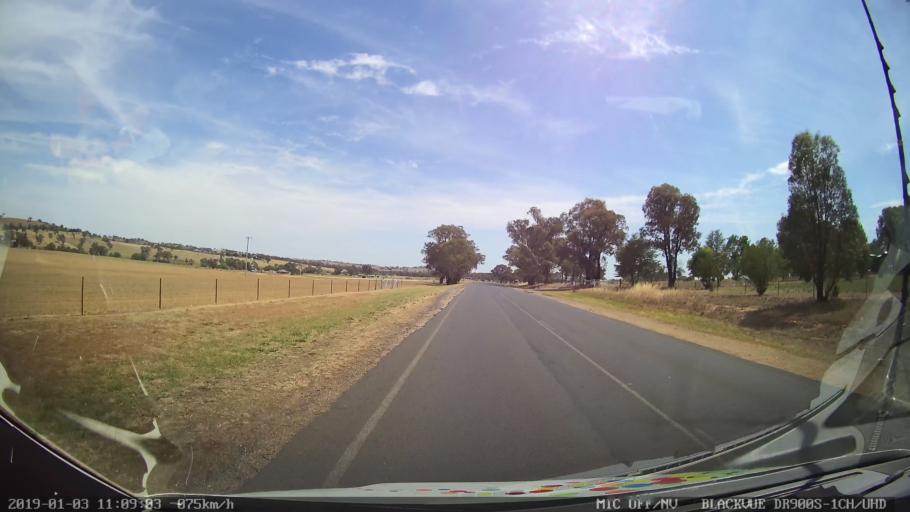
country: AU
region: New South Wales
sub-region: Young
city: Young
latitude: -34.2428
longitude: 148.2555
